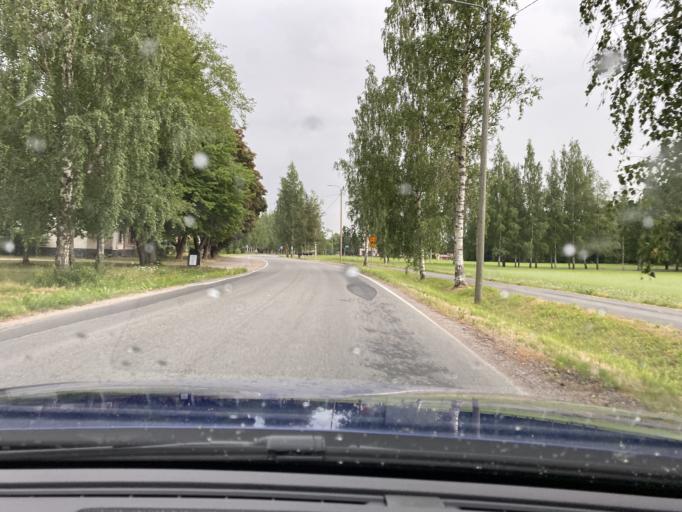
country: FI
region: Satakunta
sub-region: Rauma
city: Eura
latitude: 61.1377
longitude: 22.1252
